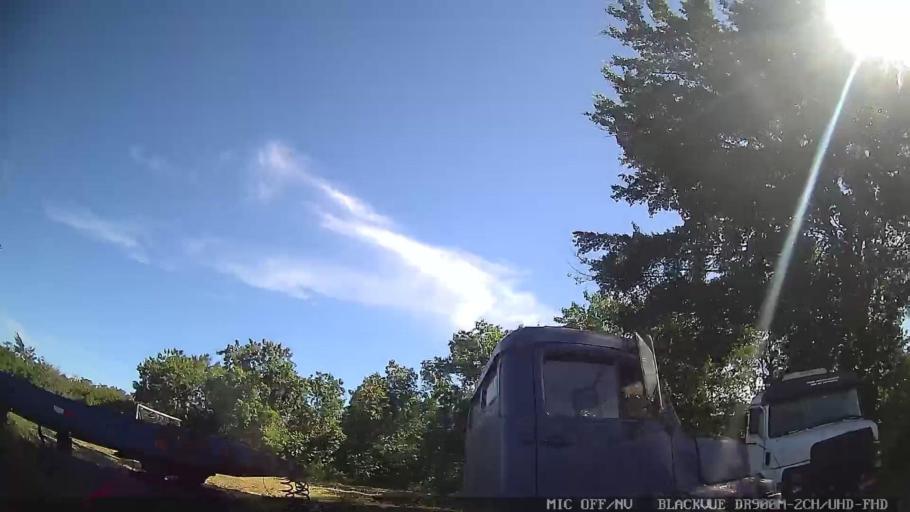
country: BR
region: Sao Paulo
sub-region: Santos
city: Santos
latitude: -23.9345
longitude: -46.2895
